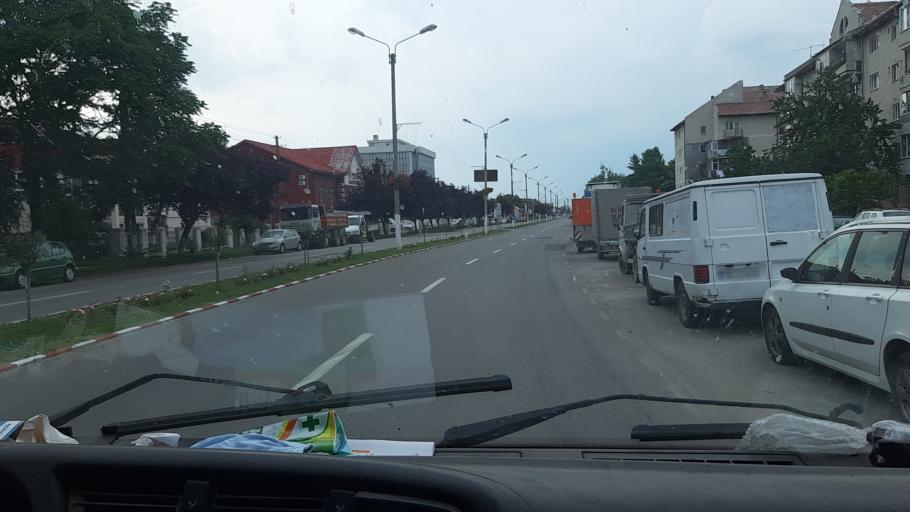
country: RO
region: Timis
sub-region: Municipiul Lugoj
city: Lugoj
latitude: 45.6980
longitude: 21.8966
